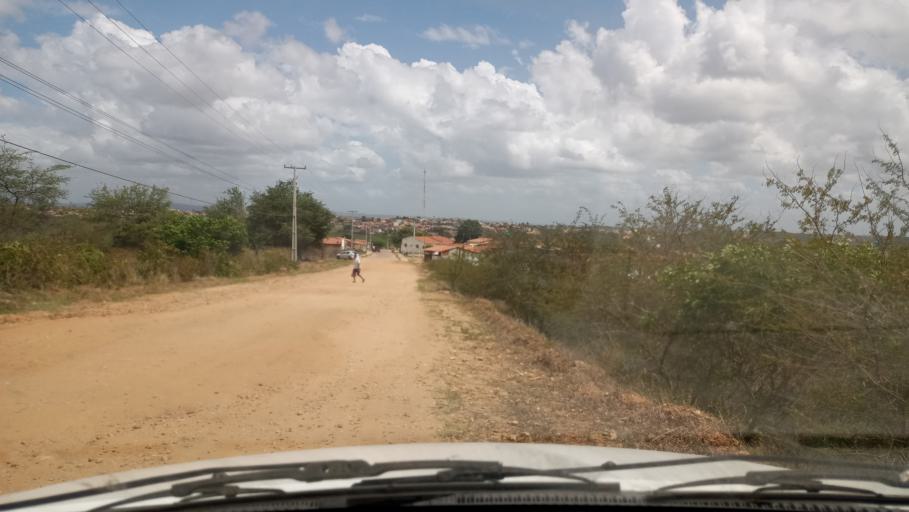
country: BR
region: Rio Grande do Norte
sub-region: Sao Paulo Do Potengi
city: Sao Paulo do Potengi
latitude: -5.9059
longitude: -35.7611
